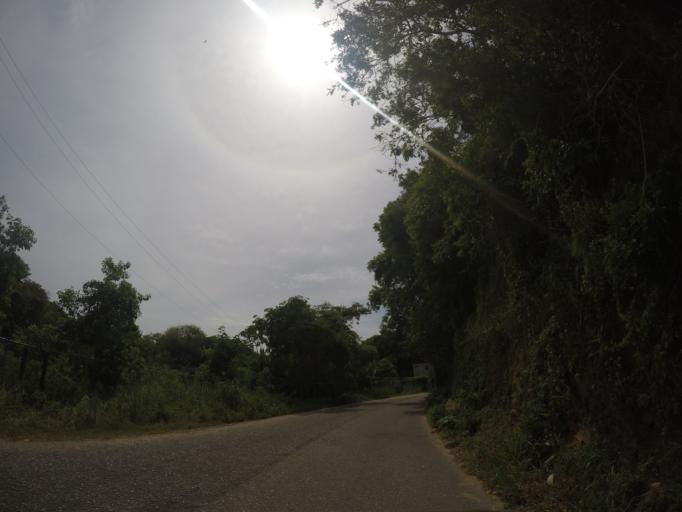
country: MX
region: Oaxaca
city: Santa Maria Tonameca
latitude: 15.6661
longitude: -96.5278
